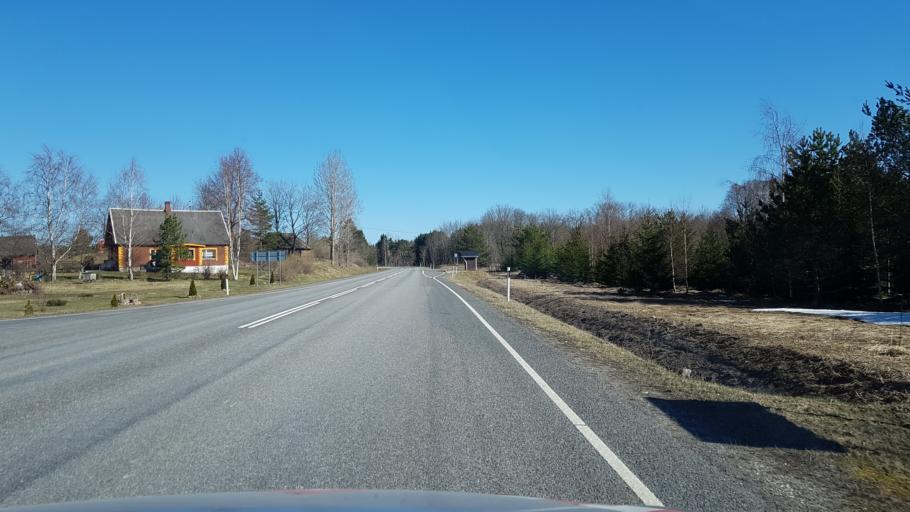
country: EE
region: Ida-Virumaa
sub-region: Aseri vald
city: Aseri
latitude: 59.3490
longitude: 26.7594
